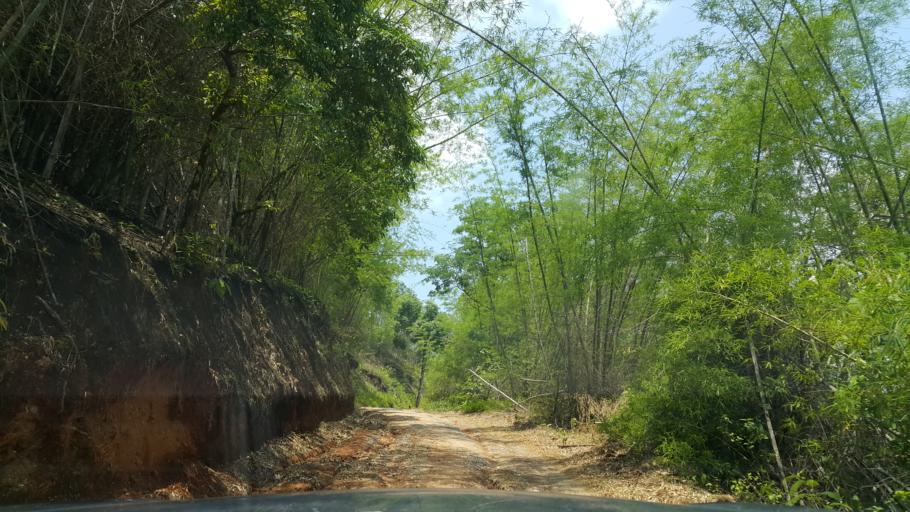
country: TH
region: Chiang Rai
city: Chiang Rai
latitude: 19.9997
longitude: 99.7144
